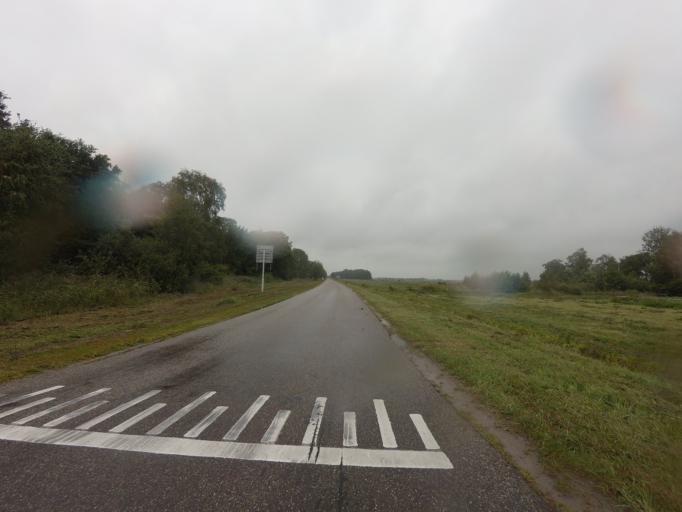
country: NL
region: Friesland
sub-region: Gemeente Tytsjerksteradiel
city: Garyp
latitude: 53.1316
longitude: 5.9589
